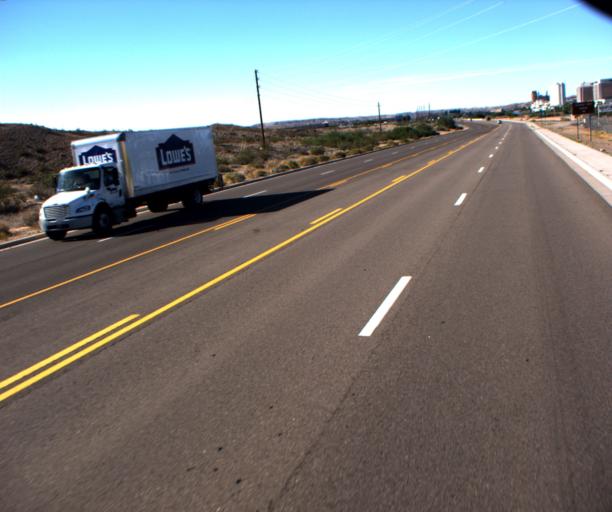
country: US
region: Nevada
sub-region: Clark County
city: Laughlin
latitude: 35.1783
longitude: -114.5650
